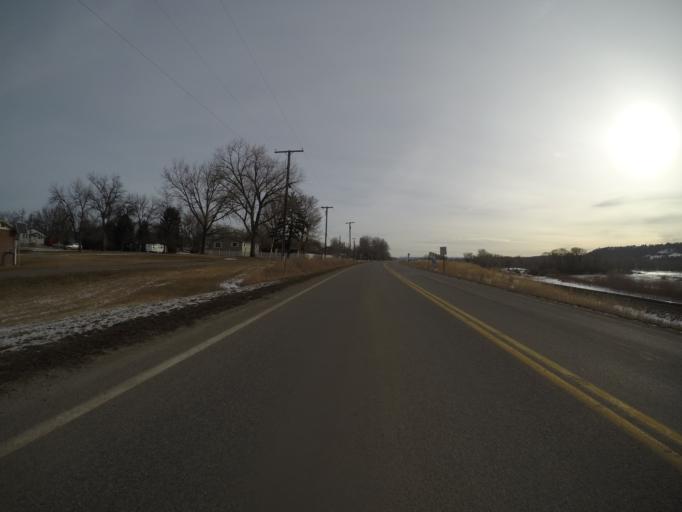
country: US
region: Montana
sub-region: Stillwater County
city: Columbus
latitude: 45.6400
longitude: -109.2643
